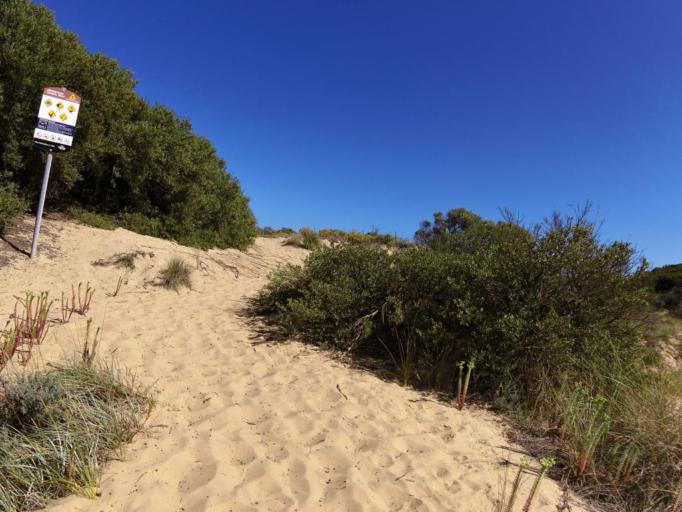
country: AU
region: Victoria
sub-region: Bass Coast
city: North Wonthaggi
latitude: -38.5395
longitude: 145.4386
